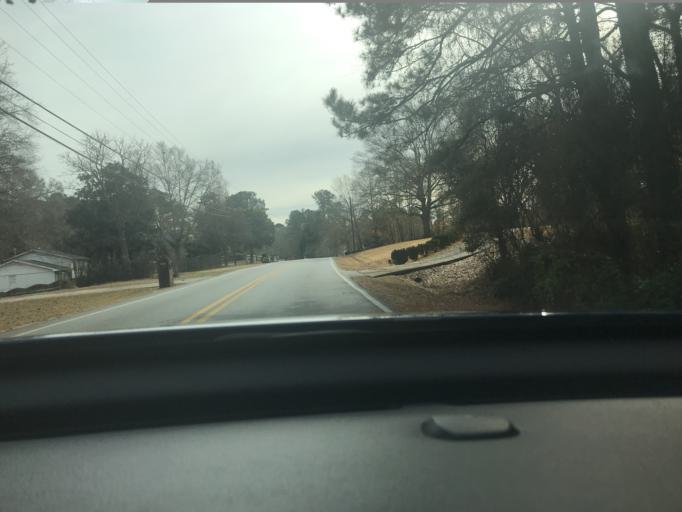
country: US
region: Georgia
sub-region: Gwinnett County
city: Lilburn
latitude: 33.9019
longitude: -84.1048
